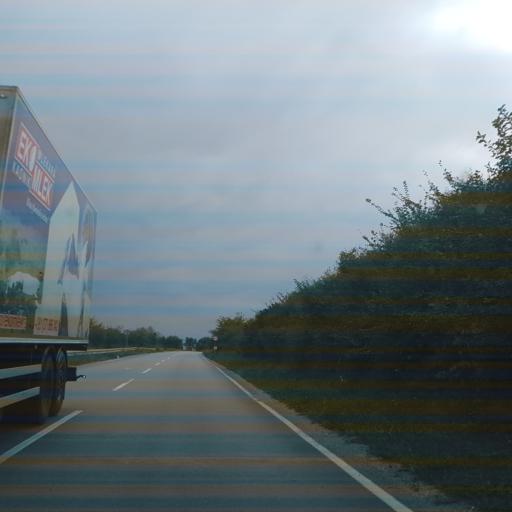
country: RS
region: Central Serbia
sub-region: Nisavski Okrug
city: Razanj
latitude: 43.6717
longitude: 21.5458
